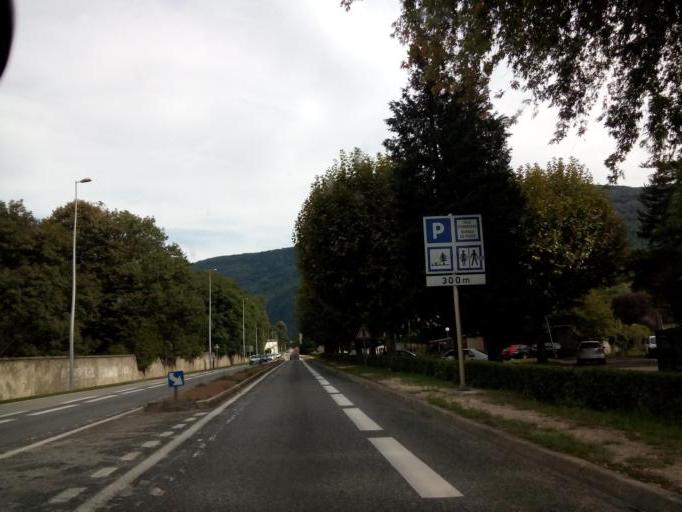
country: FR
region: Rhone-Alpes
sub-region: Departement de l'Isere
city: Notre-Dame-de-Mesage
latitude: 45.0593
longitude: 5.7680
